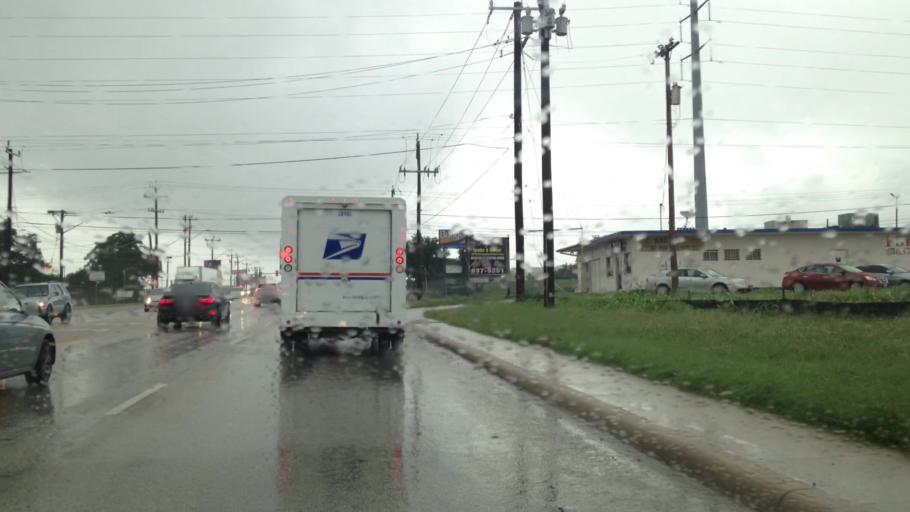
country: US
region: Texas
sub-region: Bexar County
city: Windcrest
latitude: 29.5299
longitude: -98.4110
